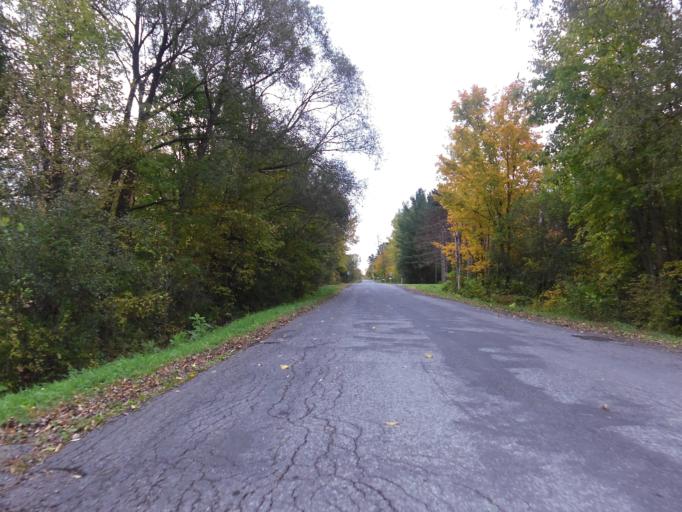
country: CA
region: Ontario
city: Arnprior
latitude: 45.4421
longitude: -76.1215
